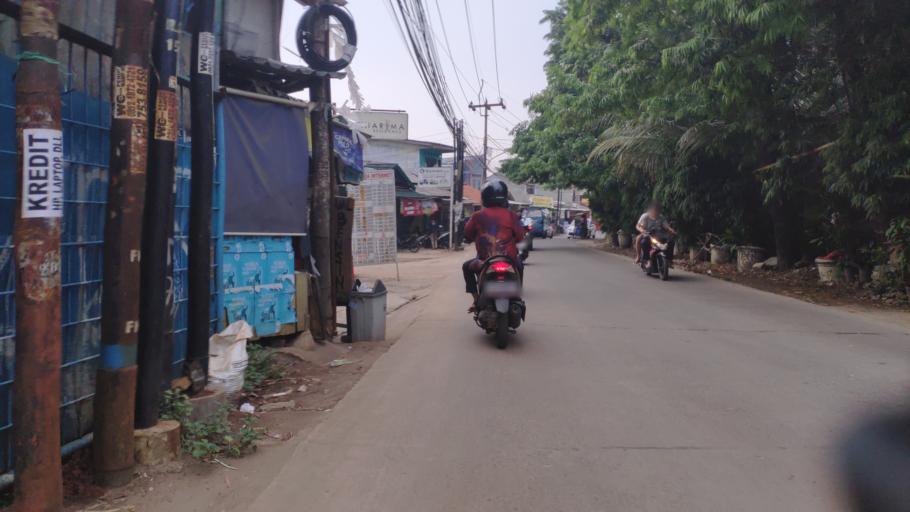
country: ID
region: West Java
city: Pamulang
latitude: -6.3262
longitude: 106.7956
